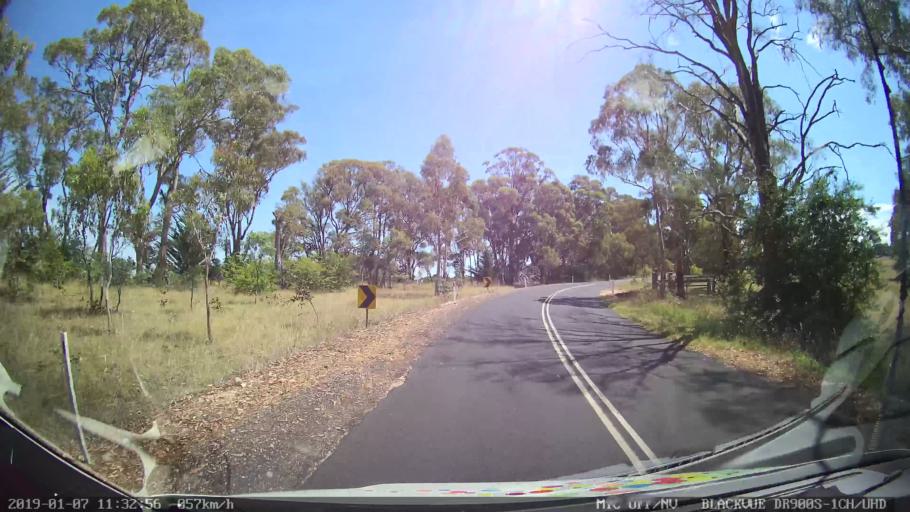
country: AU
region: New South Wales
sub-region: Armidale Dumaresq
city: Armidale
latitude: -30.4048
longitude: 151.5599
